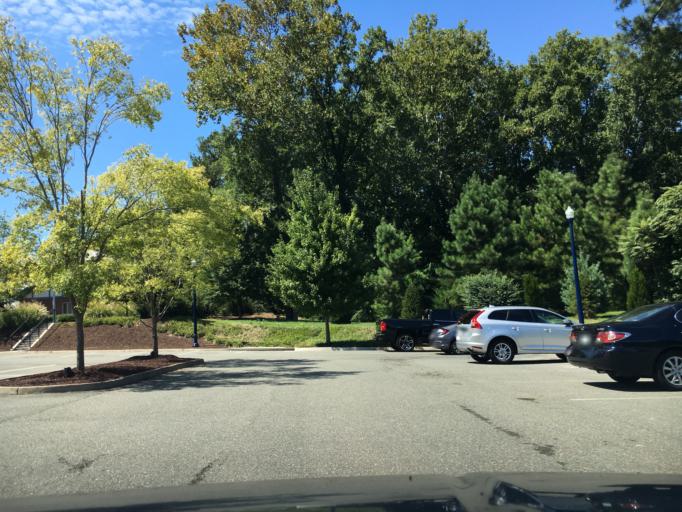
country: US
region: Virginia
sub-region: Henrico County
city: Tuckahoe
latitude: 37.5761
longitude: -77.5443
